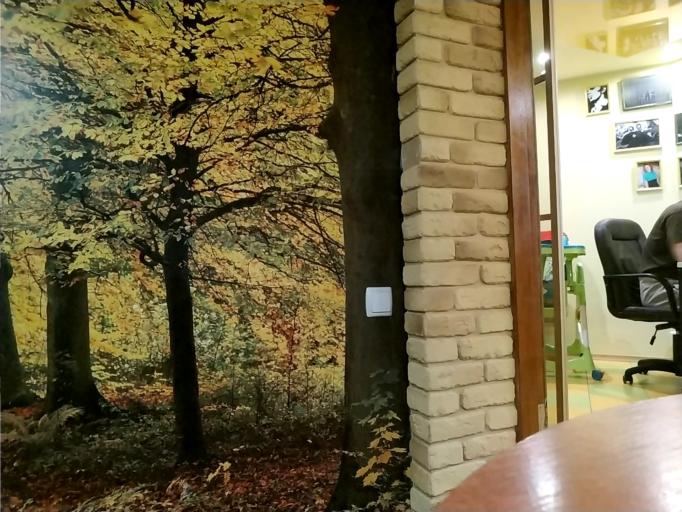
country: RU
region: Tverskaya
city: Zapadnaya Dvina
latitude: 56.3334
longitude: 31.8789
